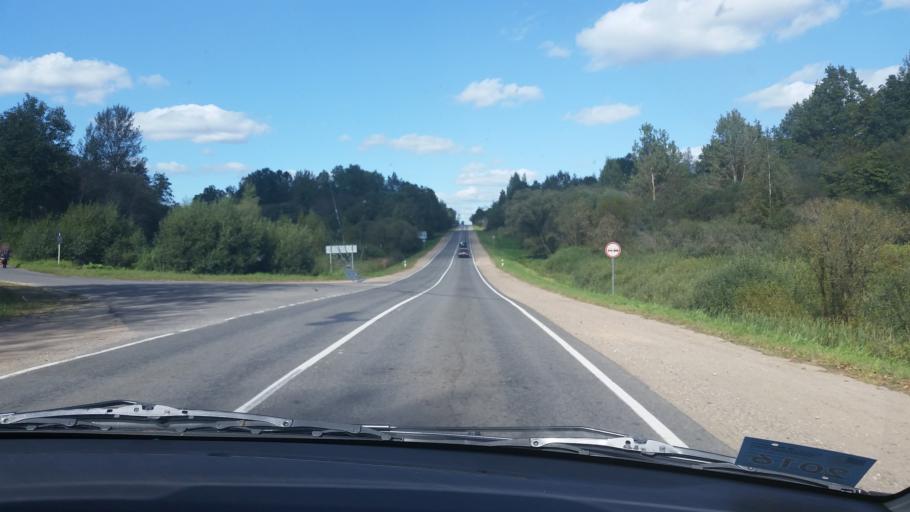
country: BY
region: Vitebsk
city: Vitebsk
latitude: 55.1052
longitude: 30.2841
